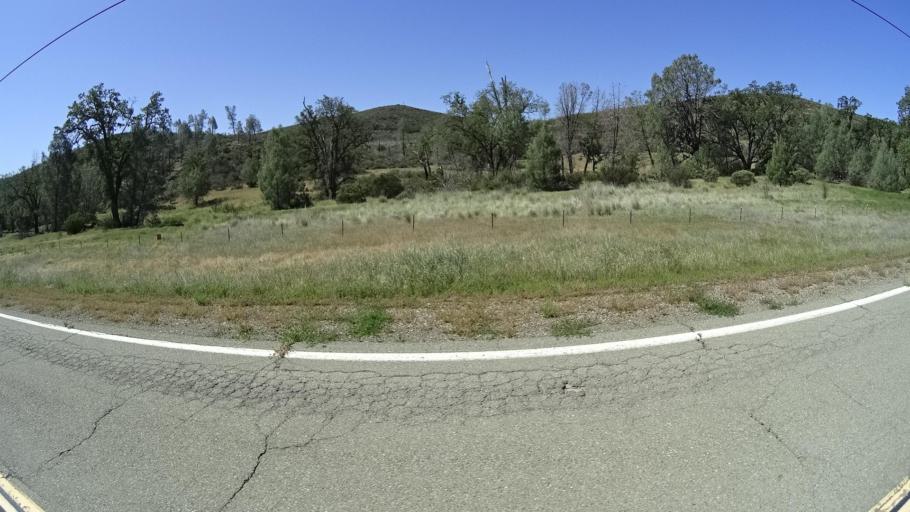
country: US
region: California
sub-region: Lake County
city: Hidden Valley Lake
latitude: 38.8570
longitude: -122.4044
